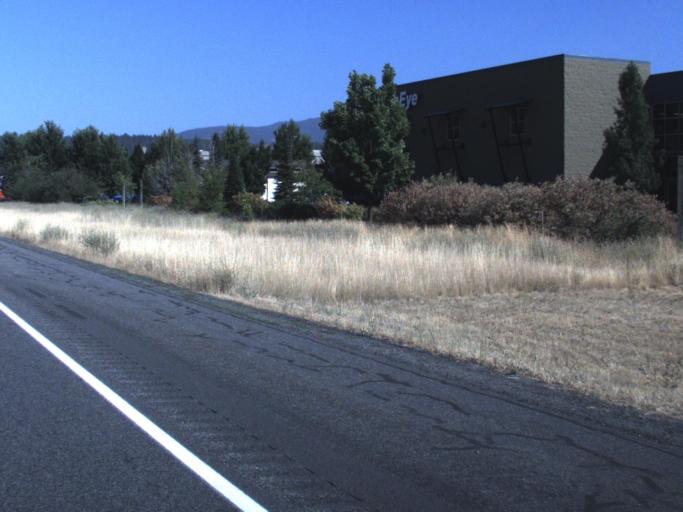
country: US
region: Washington
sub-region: Spokane County
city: Liberty Lake
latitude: 47.6801
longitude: -117.0925
